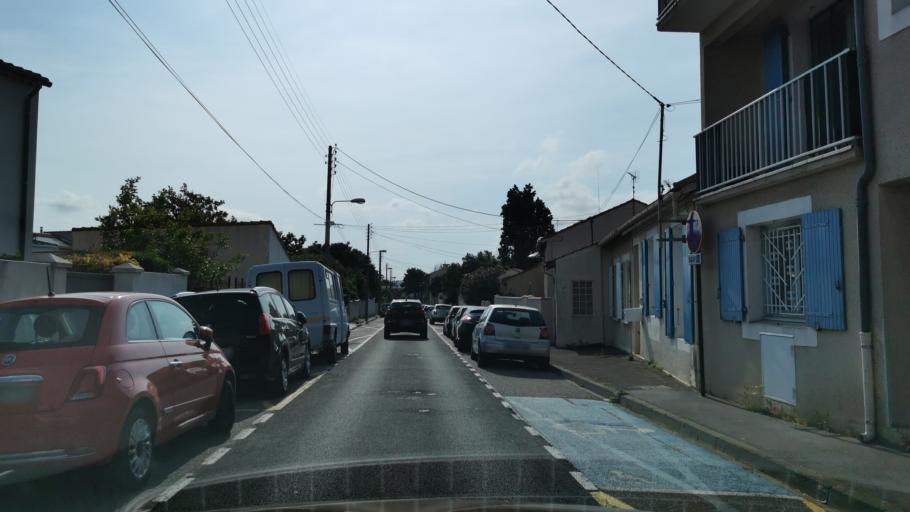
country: FR
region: Languedoc-Roussillon
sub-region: Departement de l'Aude
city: Narbonne
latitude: 43.1876
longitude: 3.0134
